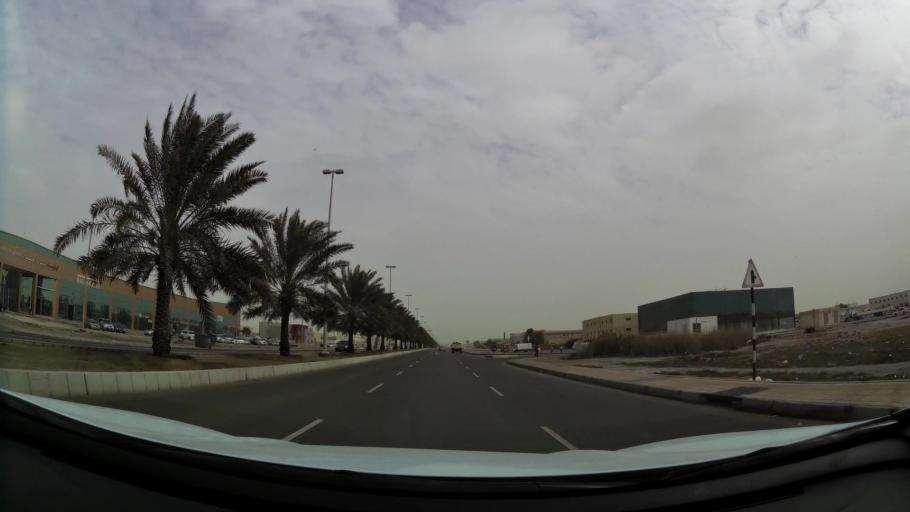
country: AE
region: Abu Dhabi
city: Abu Dhabi
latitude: 24.3446
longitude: 54.4745
